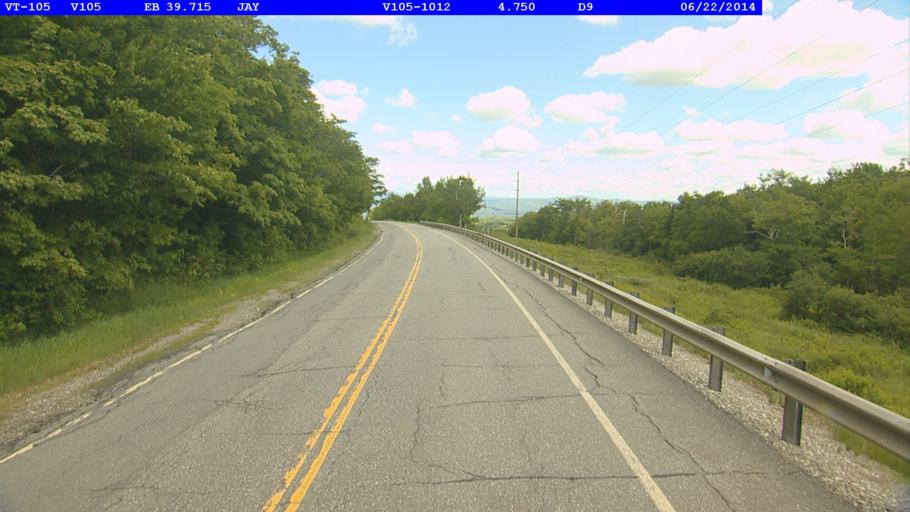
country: CA
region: Quebec
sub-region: Monteregie
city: Sutton
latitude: 44.9821
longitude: -72.4896
